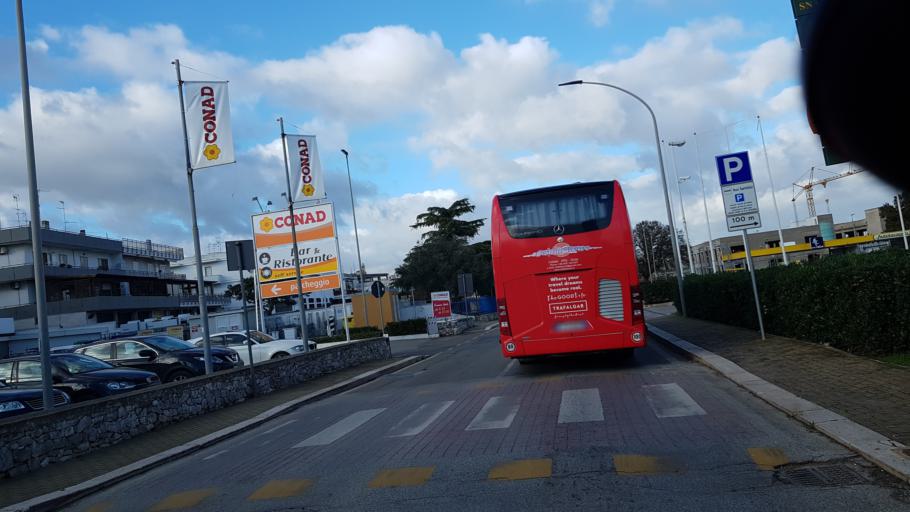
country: IT
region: Apulia
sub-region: Provincia di Bari
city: Alberobello
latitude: 40.7857
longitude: 17.2446
